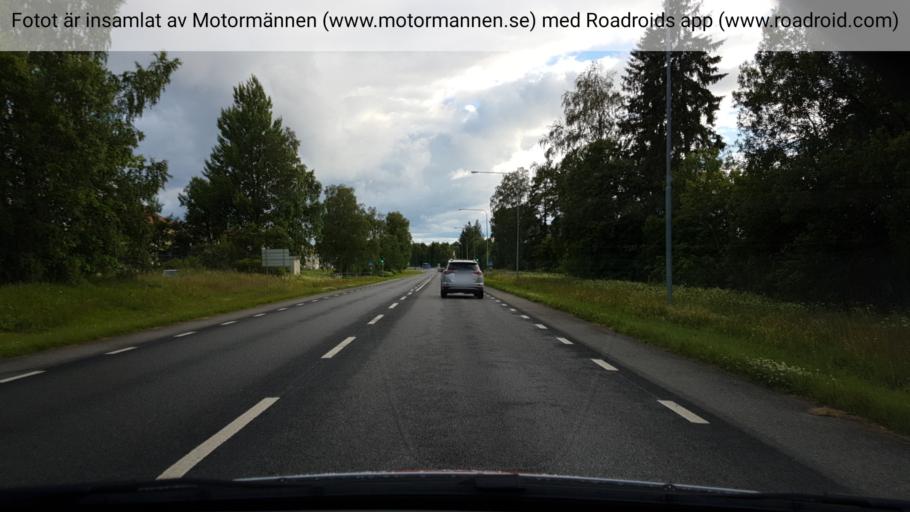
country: SE
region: OErebro
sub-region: Hallefors Kommun
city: Haellefors
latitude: 59.7796
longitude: 14.5287
